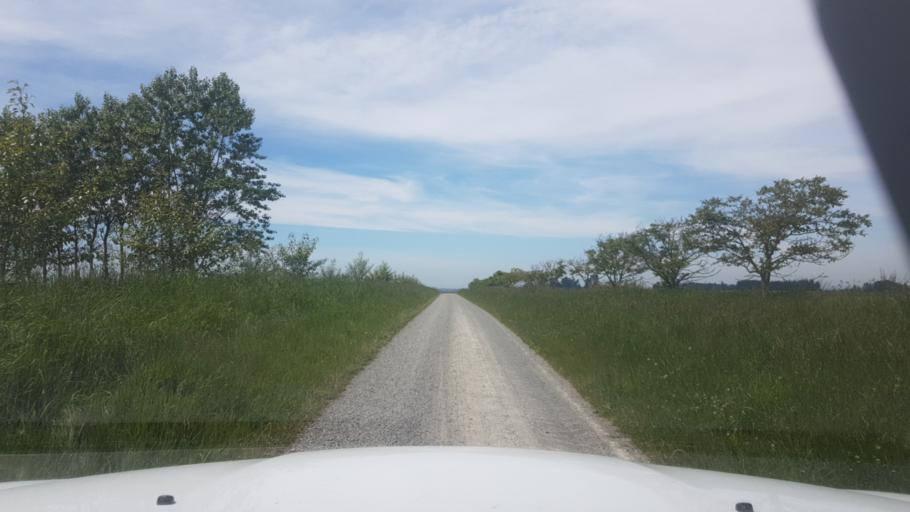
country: NZ
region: Canterbury
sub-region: Timaru District
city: Pleasant Point
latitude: -44.2060
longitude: 171.0368
